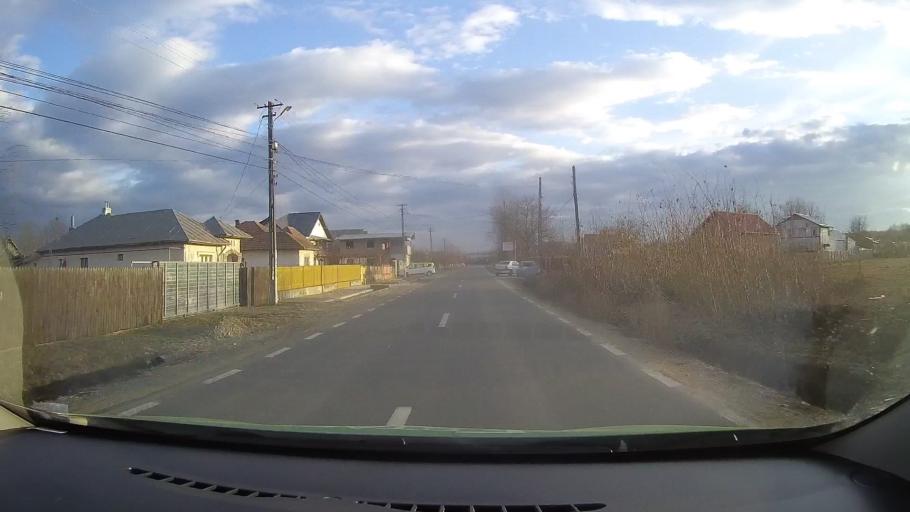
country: RO
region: Dambovita
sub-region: Comuna I. L. Caragiale
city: Ghirdoveni
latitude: 44.9548
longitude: 25.6577
